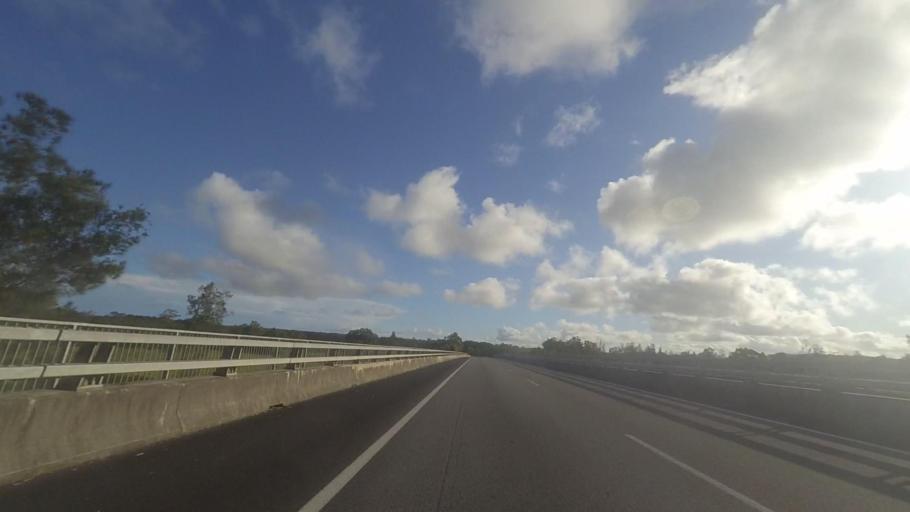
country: AU
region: New South Wales
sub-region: Great Lakes
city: Nabiac
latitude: -32.1047
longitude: 152.3743
